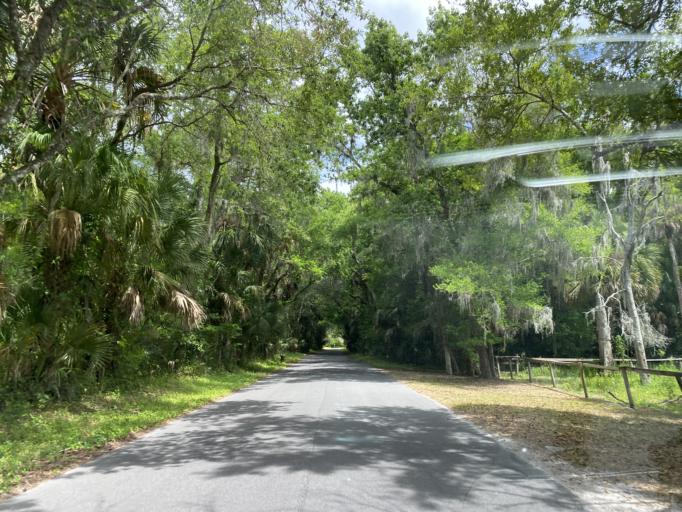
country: US
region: Florida
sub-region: Volusia County
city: DeBary
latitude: 28.8350
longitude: -81.3354
